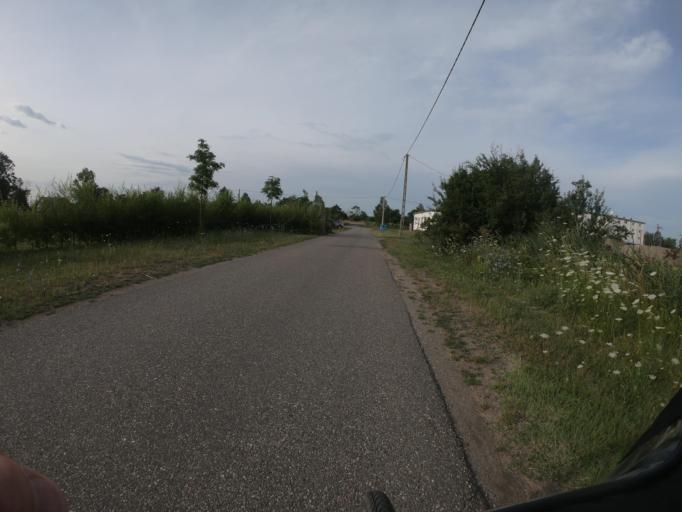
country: HU
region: Hajdu-Bihar
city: Hortobagy
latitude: 47.6053
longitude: 21.0726
